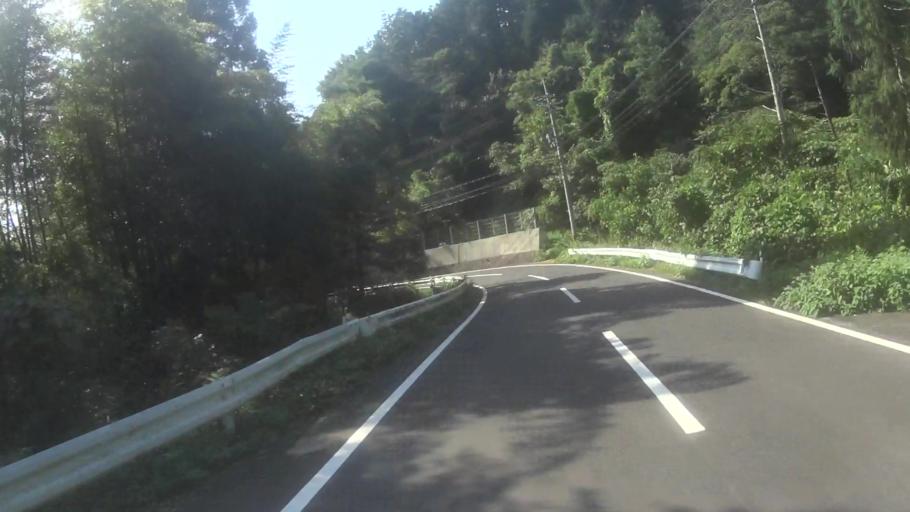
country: JP
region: Kyoto
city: Miyazu
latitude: 35.6894
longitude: 135.1180
